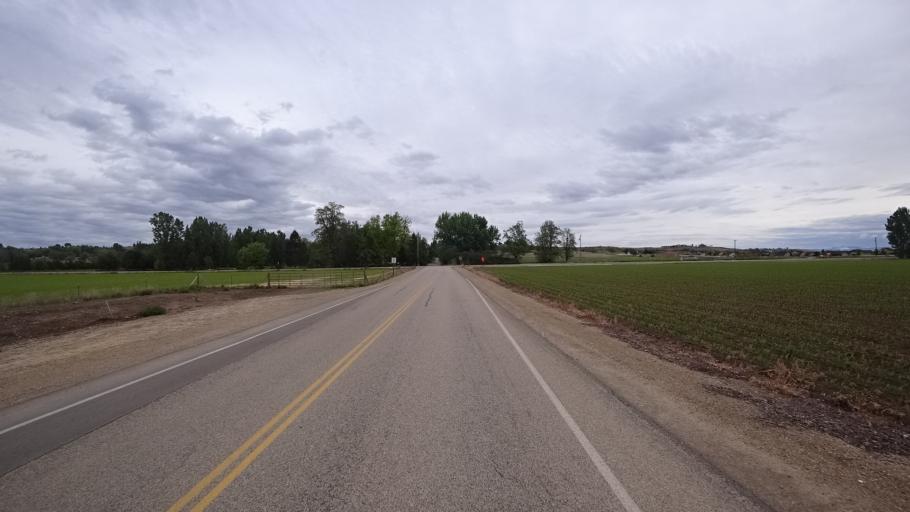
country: US
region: Idaho
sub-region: Ada County
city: Star
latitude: 43.7167
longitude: -116.5031
